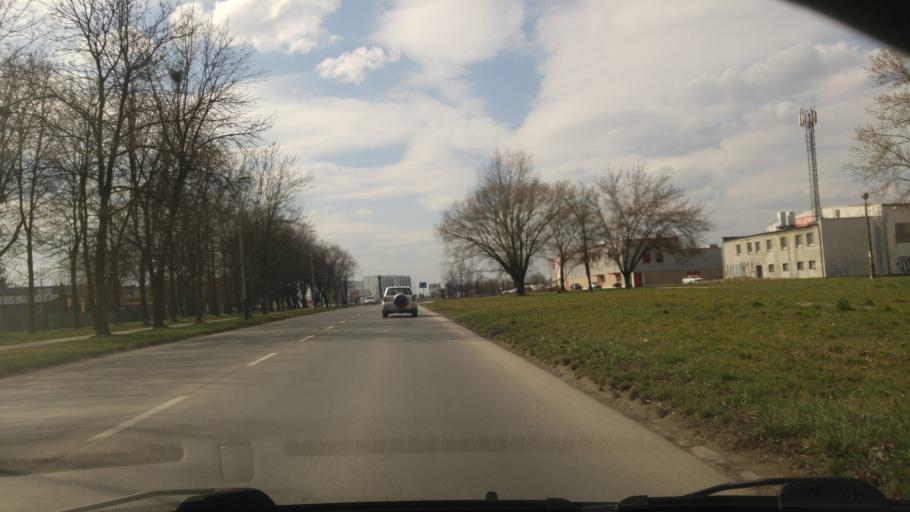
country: PL
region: Lesser Poland Voivodeship
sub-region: Powiat krakowski
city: Michalowice
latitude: 50.0906
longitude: 20.0087
